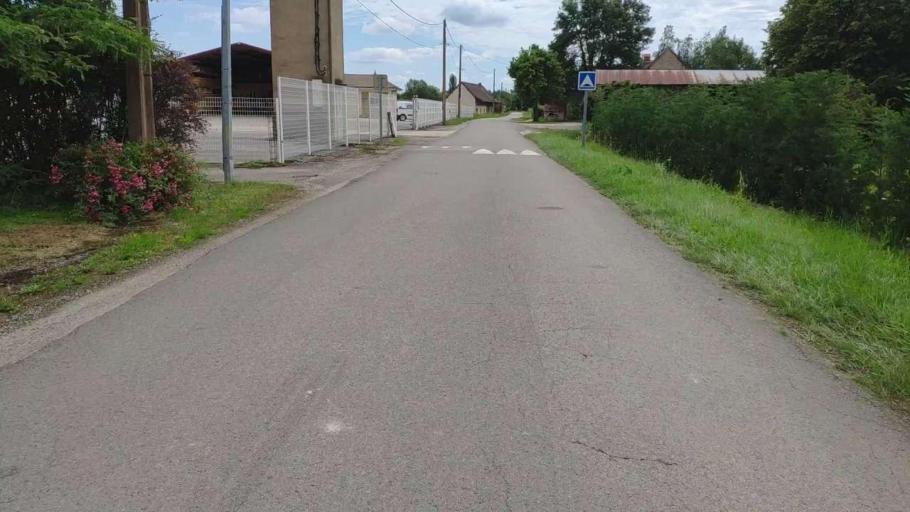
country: FR
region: Franche-Comte
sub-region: Departement du Jura
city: Chaussin
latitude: 46.8786
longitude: 5.4353
